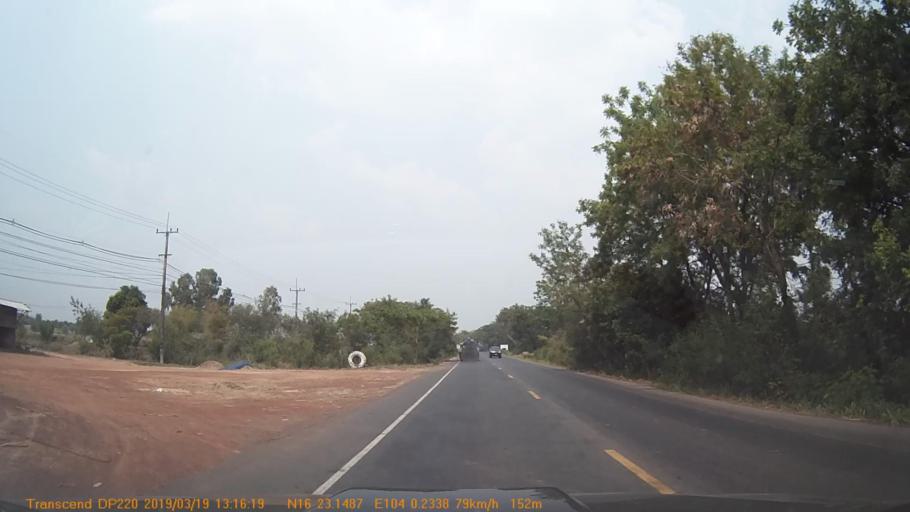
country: TH
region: Roi Et
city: Waeng
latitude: 16.3863
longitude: 104.0041
